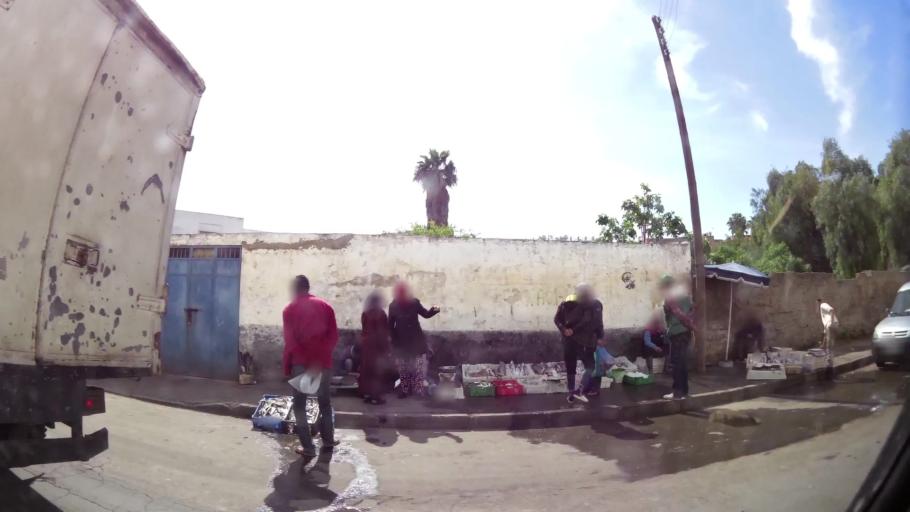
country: MA
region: Grand Casablanca
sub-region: Casablanca
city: Casablanca
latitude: 33.5858
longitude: -7.5847
